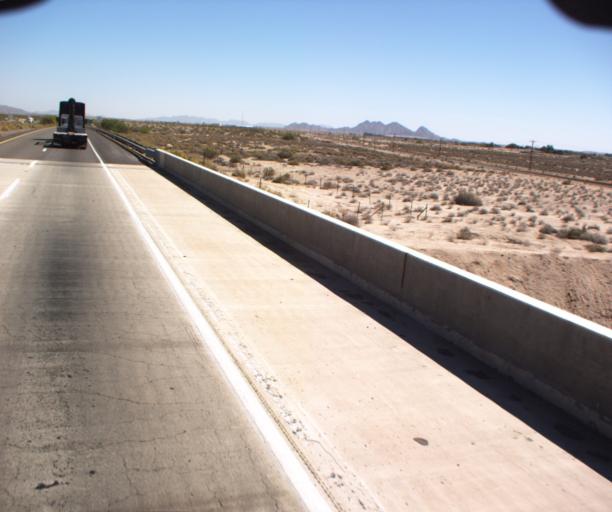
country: US
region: Arizona
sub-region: Yuma County
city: Wellton
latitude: 32.6645
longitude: -114.1303
